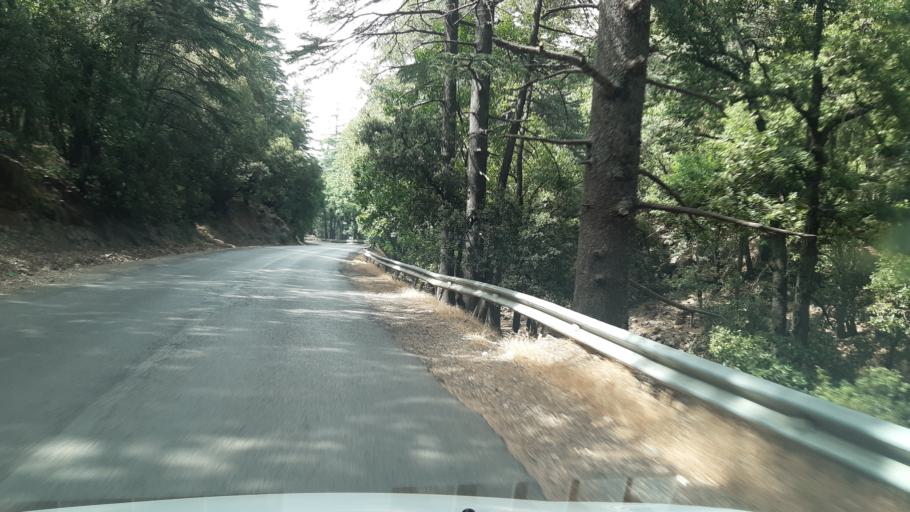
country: MA
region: Meknes-Tafilalet
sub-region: Ifrane
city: Azrou
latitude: 33.4293
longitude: -5.1741
